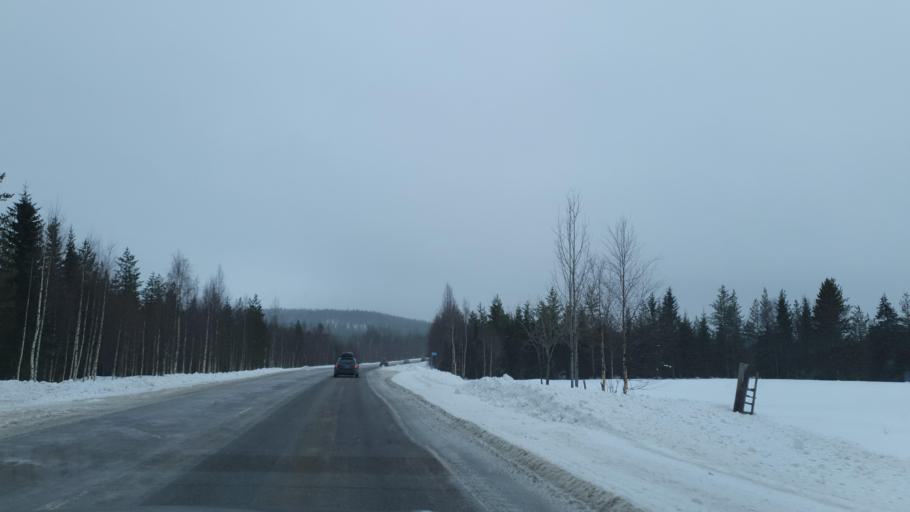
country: FI
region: Lapland
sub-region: Torniolaakso
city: Pello
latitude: 66.9890
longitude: 24.0502
